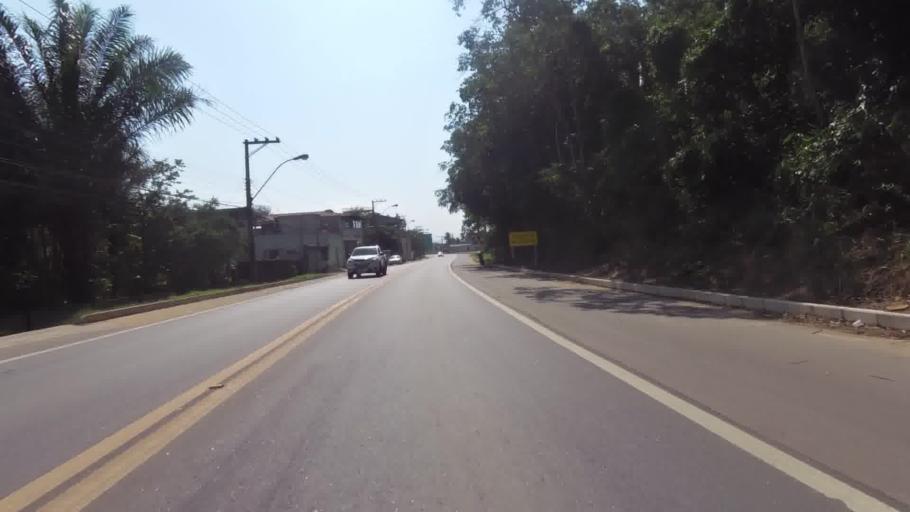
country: BR
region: Espirito Santo
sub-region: Piuma
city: Piuma
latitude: -20.8172
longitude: -40.6290
